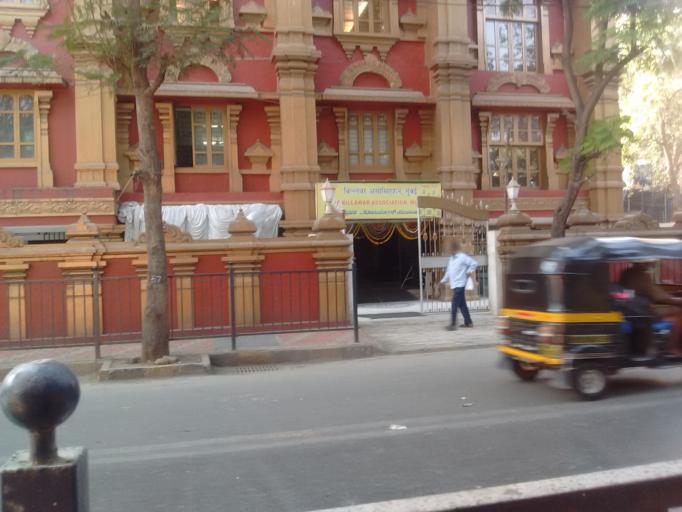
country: IN
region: Maharashtra
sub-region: Mumbai Suburban
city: Mumbai
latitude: 19.0809
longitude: 72.8457
